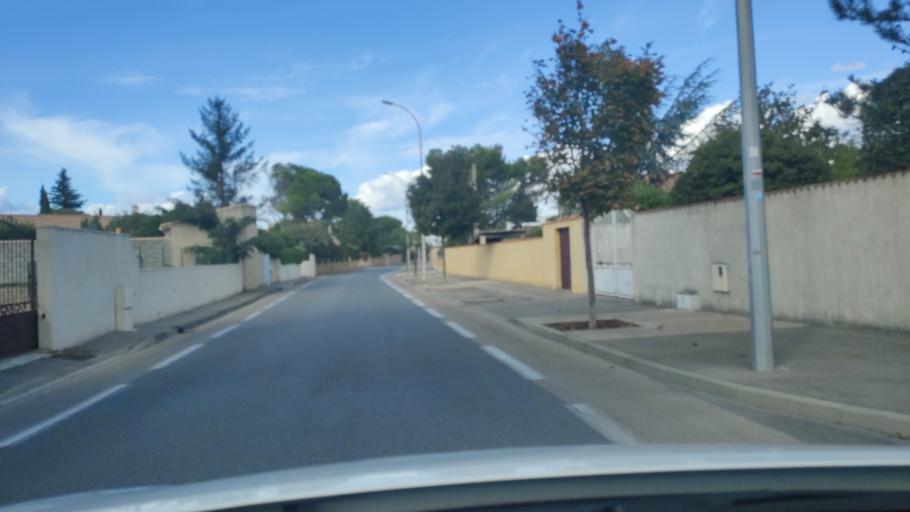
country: FR
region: Languedoc-Roussillon
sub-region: Departement du Gard
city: Villeneuve-les-Avignon
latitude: 43.9725
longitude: 4.7807
